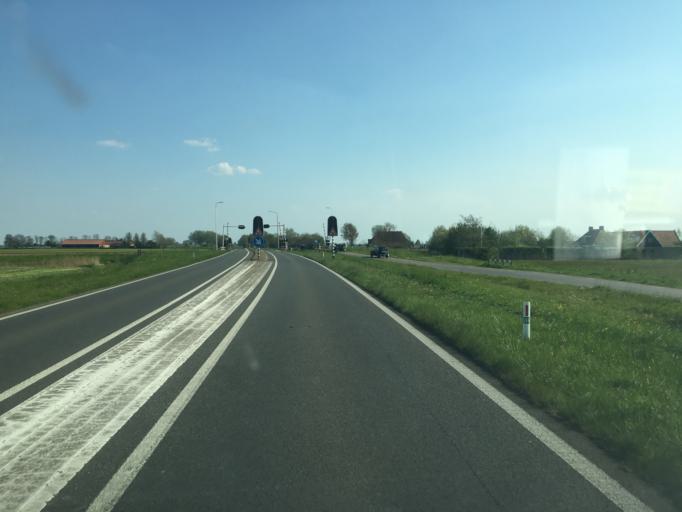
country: NL
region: Friesland
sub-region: Sudwest Fryslan
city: Workum
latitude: 52.9544
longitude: 5.4312
